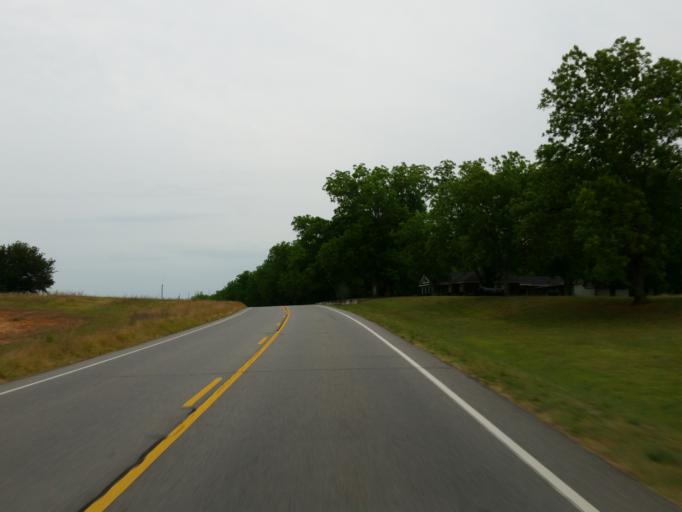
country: US
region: Georgia
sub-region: Dooly County
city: Unadilla
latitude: 32.2192
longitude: -83.7590
